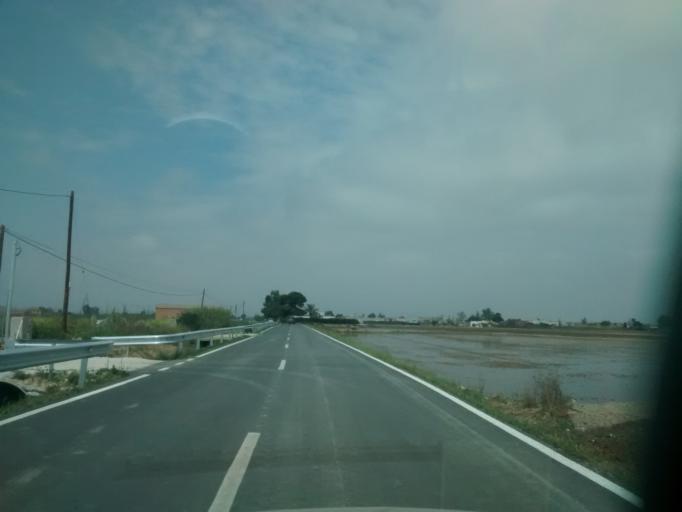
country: ES
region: Catalonia
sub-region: Provincia de Tarragona
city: Deltebre
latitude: 40.6927
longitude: 0.7211
